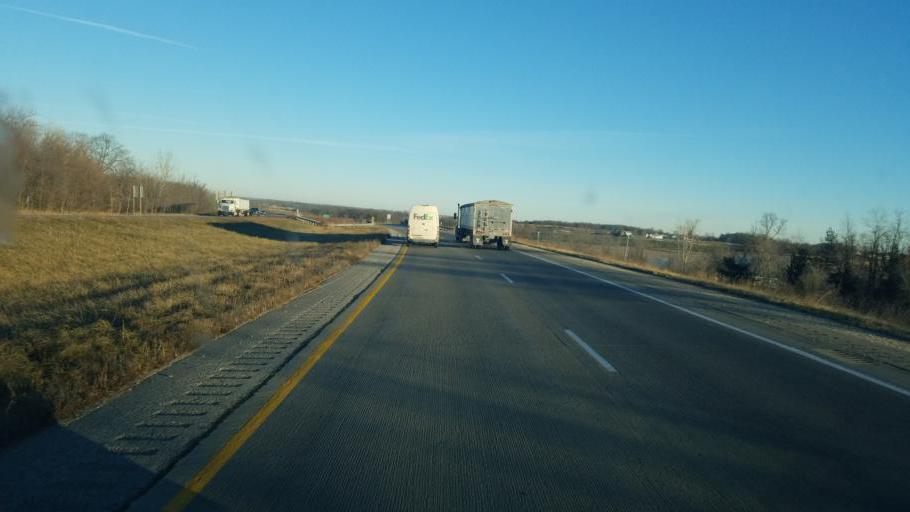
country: US
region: Iowa
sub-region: Wapello County
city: Eddyville
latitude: 41.1599
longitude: -92.6220
